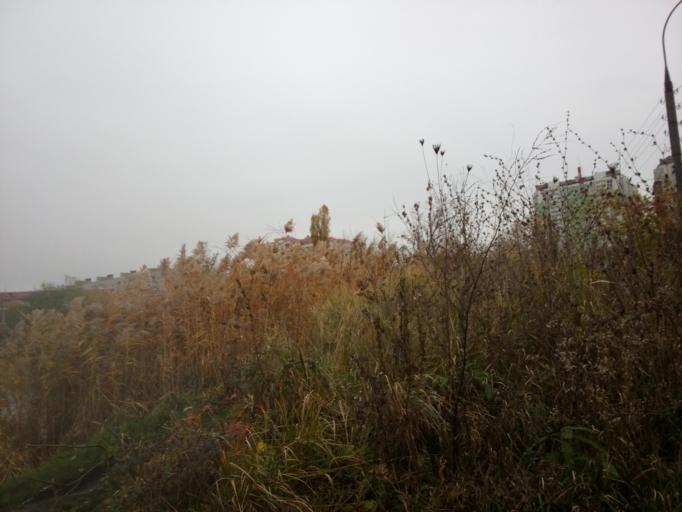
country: RU
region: Krasnodarskiy
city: Krasnodar
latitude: 45.0400
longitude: 39.0169
